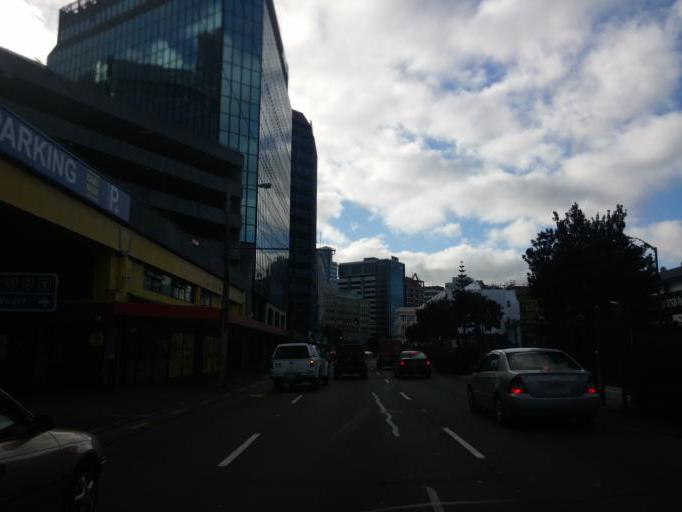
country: NZ
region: Wellington
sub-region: Wellington City
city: Wellington
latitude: -41.2866
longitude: 174.7780
